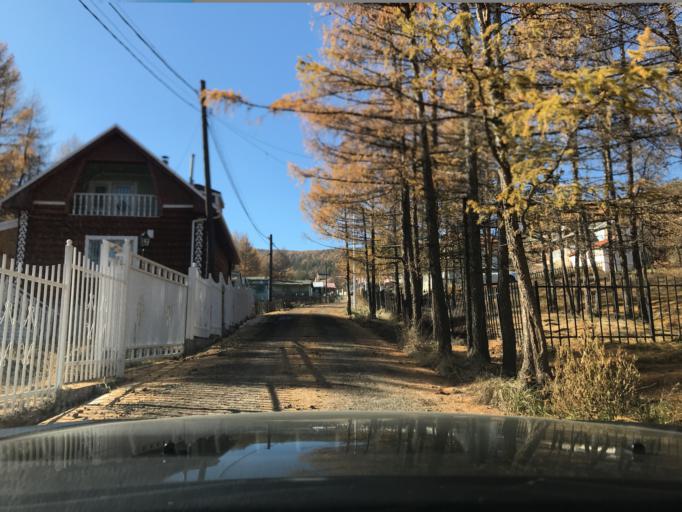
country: MN
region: Ulaanbaatar
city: Ulaanbaatar
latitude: 48.0385
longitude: 106.8884
